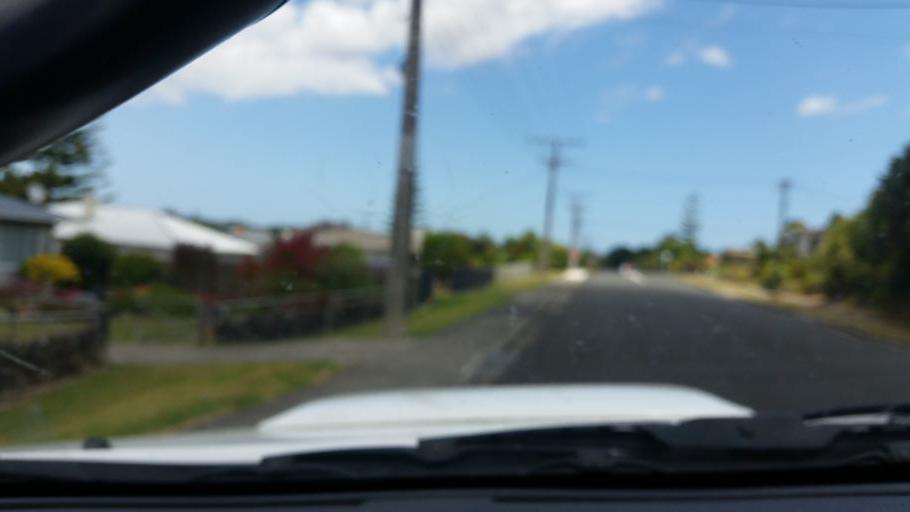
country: NZ
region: Northland
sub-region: Kaipara District
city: Dargaville
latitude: -35.9340
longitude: 173.8700
